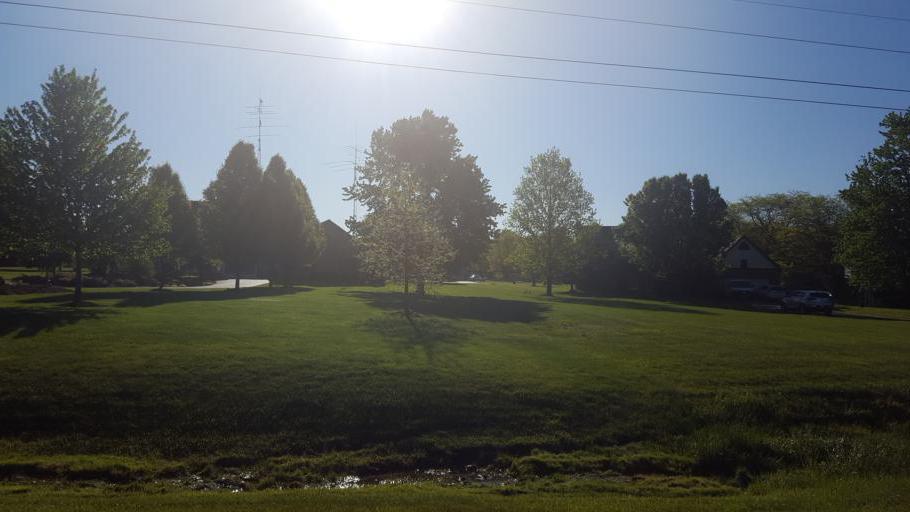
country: US
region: Ohio
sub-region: Delaware County
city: Sunbury
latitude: 40.2084
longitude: -82.8722
